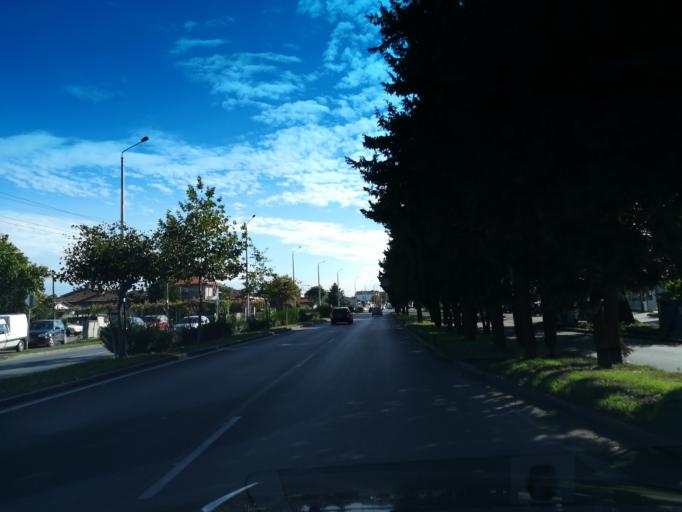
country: BG
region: Stara Zagora
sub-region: Obshtina Stara Zagora
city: Stara Zagora
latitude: 42.4036
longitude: 25.6425
